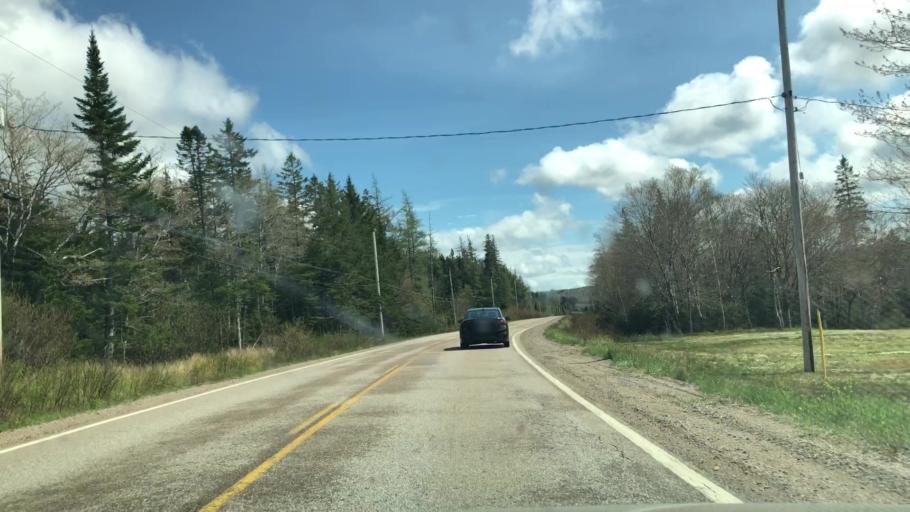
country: CA
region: Nova Scotia
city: Antigonish
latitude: 45.2097
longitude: -62.0040
